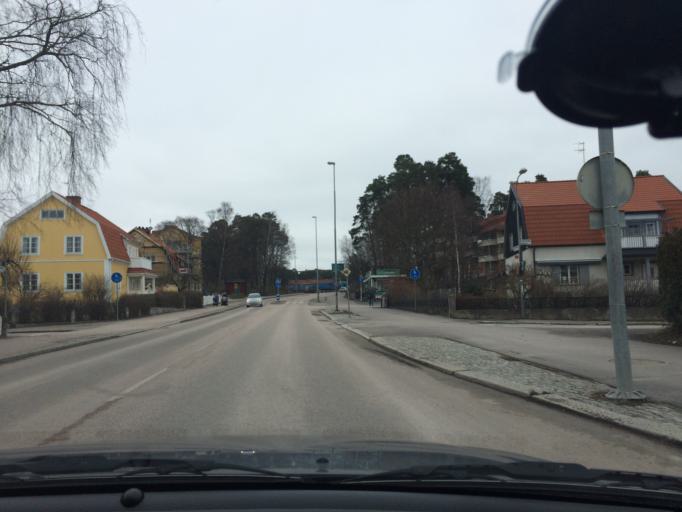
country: SE
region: Vaestmanland
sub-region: Vasteras
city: Vasteras
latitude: 59.6222
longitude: 16.5466
